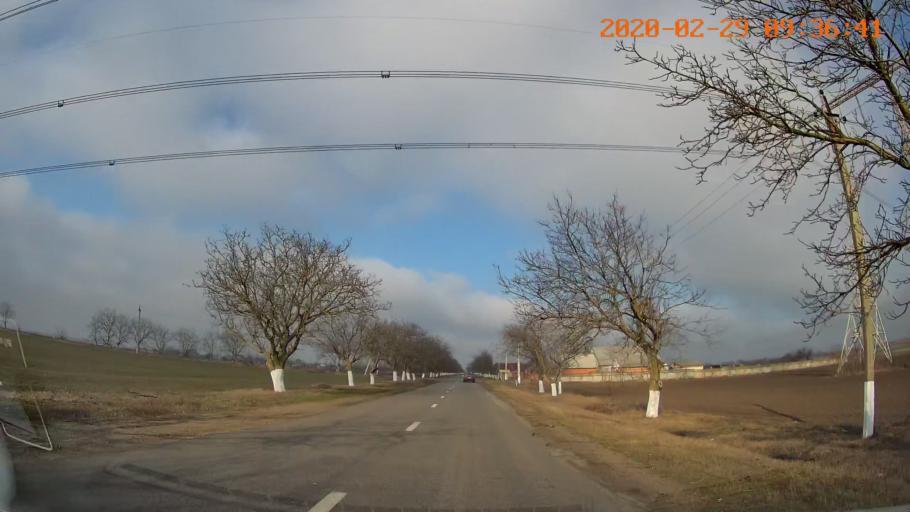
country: MD
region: Telenesti
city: Dnestrovsc
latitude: 46.6252
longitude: 29.8844
